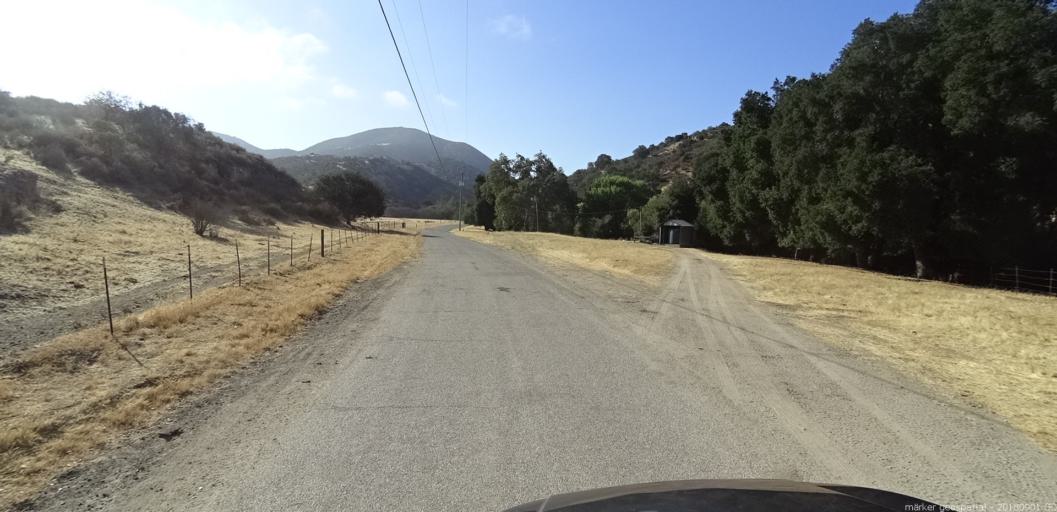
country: US
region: California
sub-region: Monterey County
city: Greenfield
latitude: 36.2407
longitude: -121.2870
